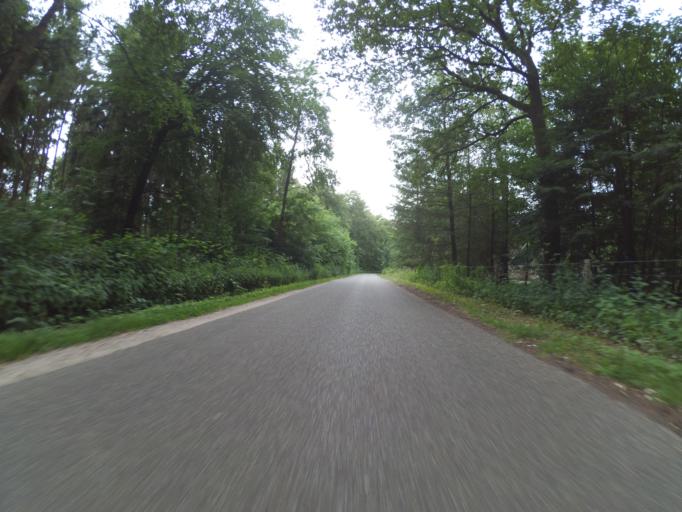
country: NL
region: Gelderland
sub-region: Gemeente Brummen
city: Eerbeek
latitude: 52.0889
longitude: 6.0362
